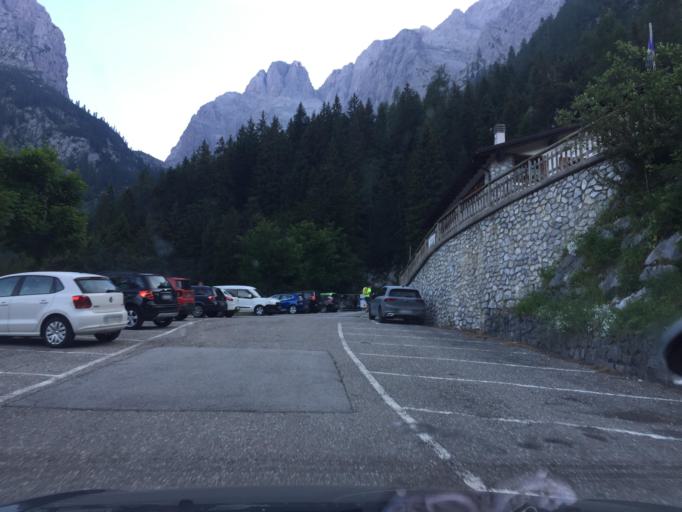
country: IT
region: Friuli Venezia Giulia
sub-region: Provincia di Udine
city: Rigolato
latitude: 46.5917
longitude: 12.8677
